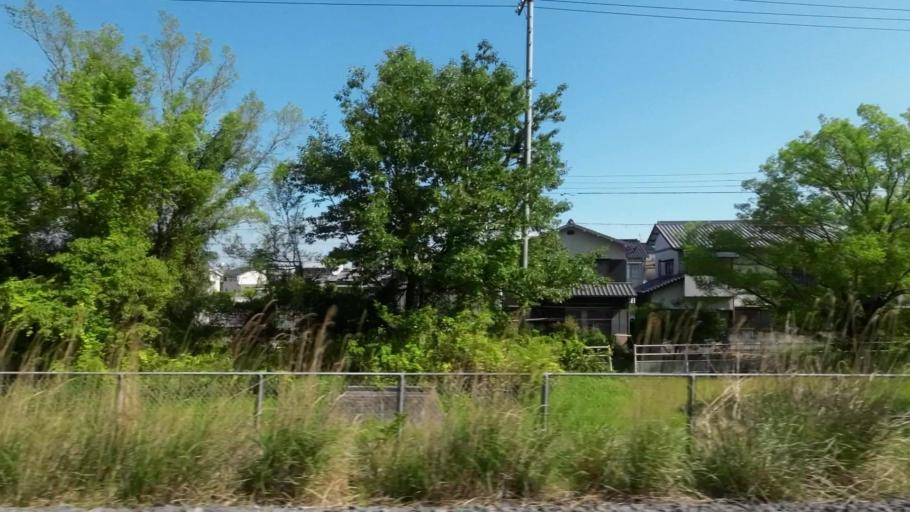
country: JP
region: Kagawa
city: Sakaidecho
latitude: 34.3146
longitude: 133.8729
